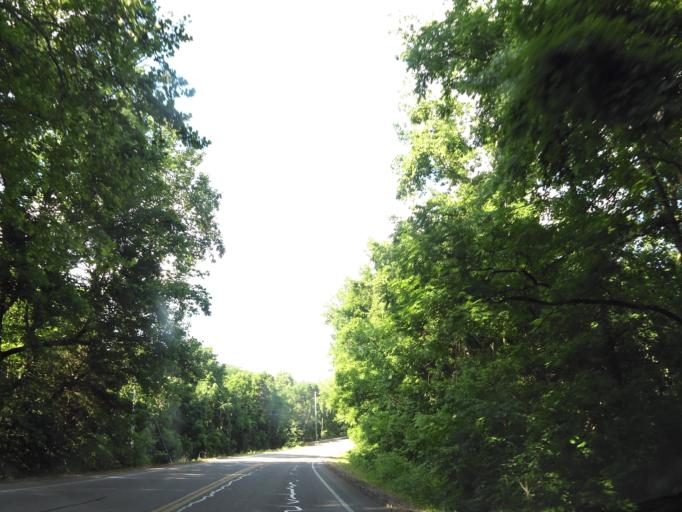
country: US
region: Tennessee
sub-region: Perry County
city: Linden
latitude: 35.6336
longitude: -87.8056
